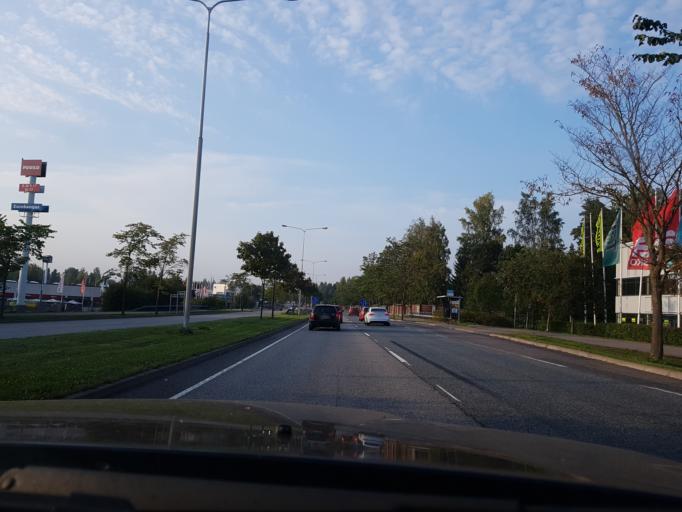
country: FI
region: Uusimaa
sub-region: Helsinki
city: Tuusula
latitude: 60.3854
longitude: 25.0255
